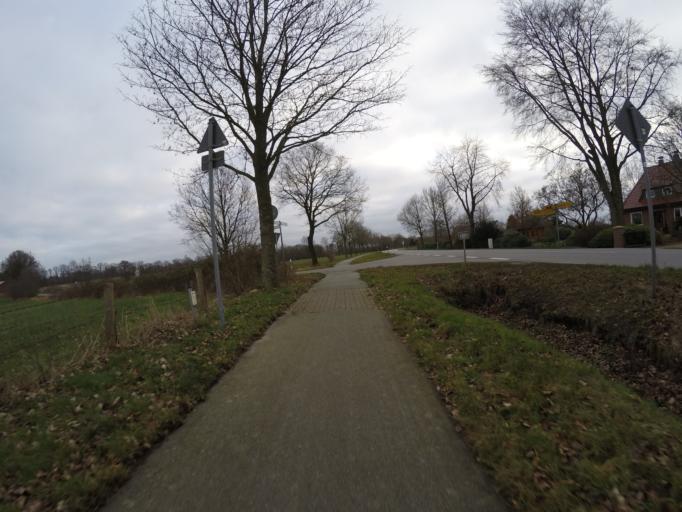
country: DE
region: Schleswig-Holstein
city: Alveslohe
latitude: 53.8002
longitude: 9.9176
